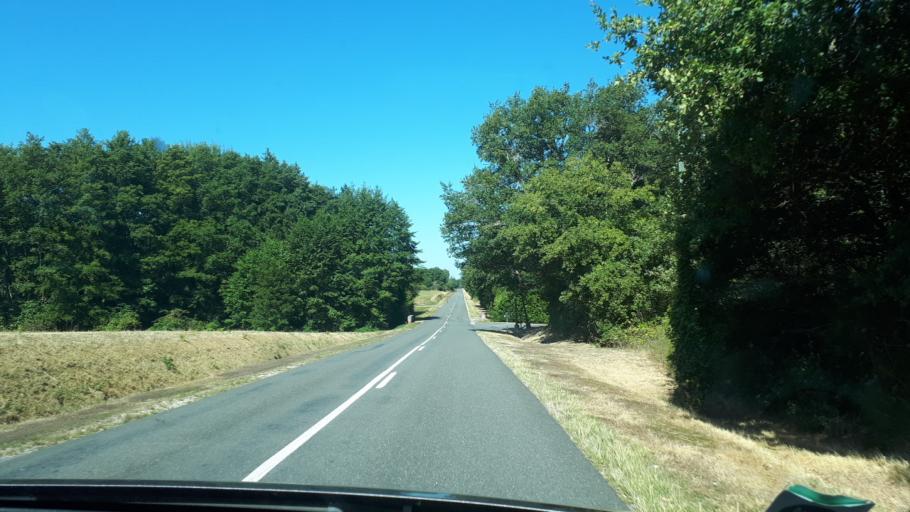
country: FR
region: Centre
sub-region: Departement du Loiret
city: Cerdon
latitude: 47.6370
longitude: 2.4185
